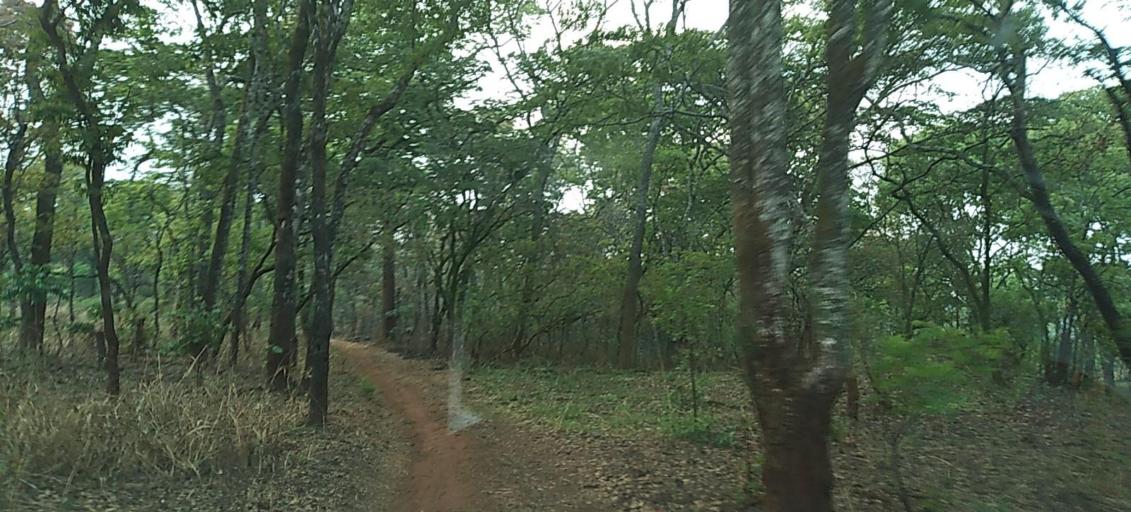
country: ZM
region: North-Western
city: Solwezi
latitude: -12.0450
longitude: 26.0135
